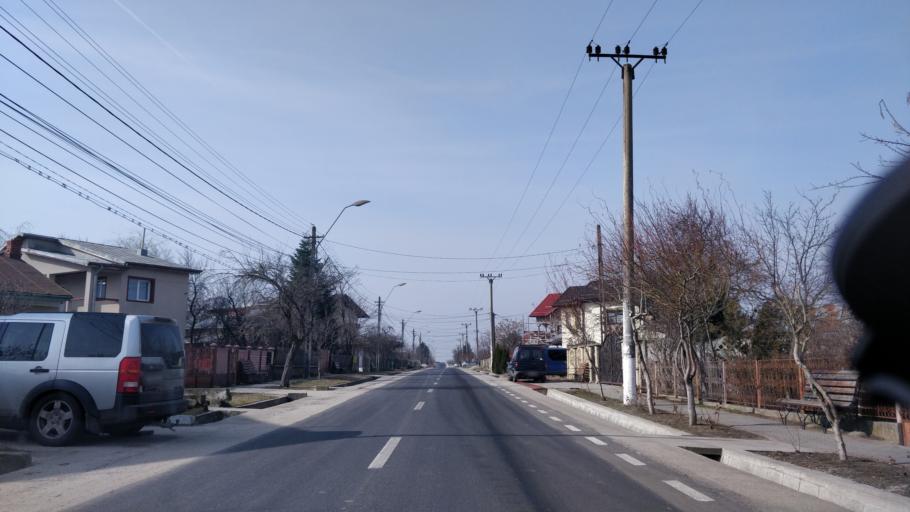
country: RO
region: Giurgiu
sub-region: Comuna Bolintin Deal
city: Bolintin Deal
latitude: 44.4612
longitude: 25.8079
